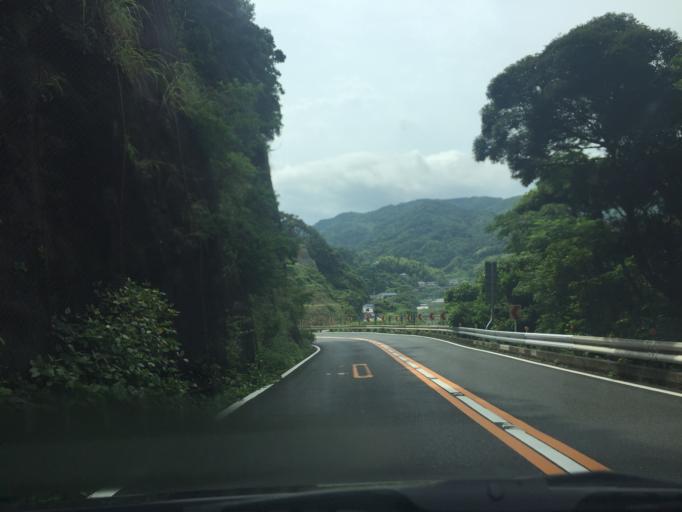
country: JP
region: Shizuoka
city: Shimoda
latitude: 34.7207
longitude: 138.9876
